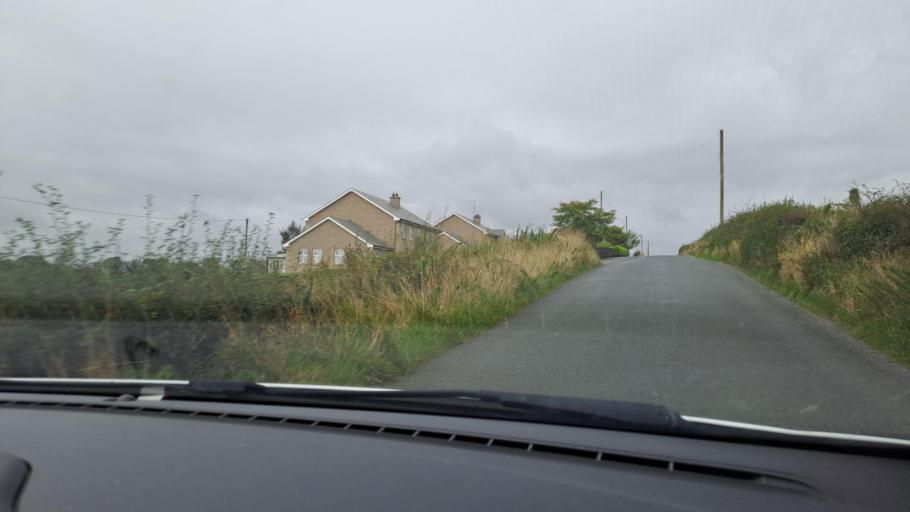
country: IE
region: Ulster
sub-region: County Monaghan
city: Carrickmacross
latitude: 54.0033
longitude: -6.8056
